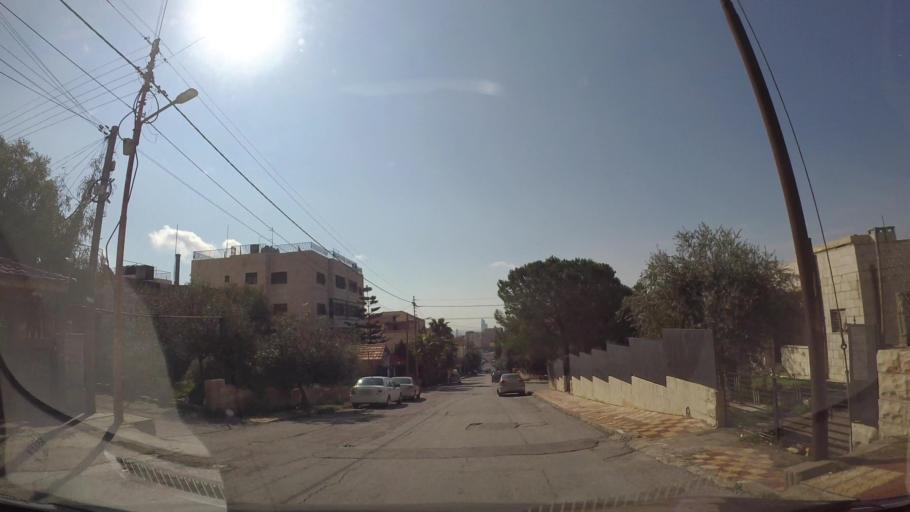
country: JO
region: Amman
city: Al Jubayhah
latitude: 31.9983
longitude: 35.8986
